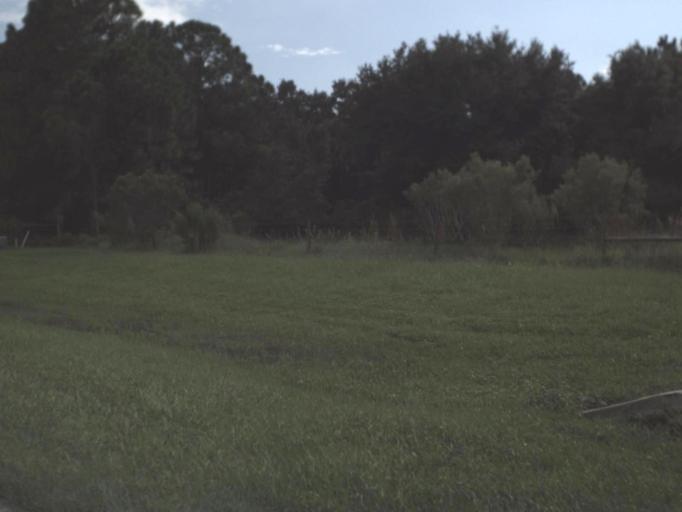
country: US
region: Florida
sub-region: Sarasota County
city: Plantation
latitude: 27.0729
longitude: -82.3261
